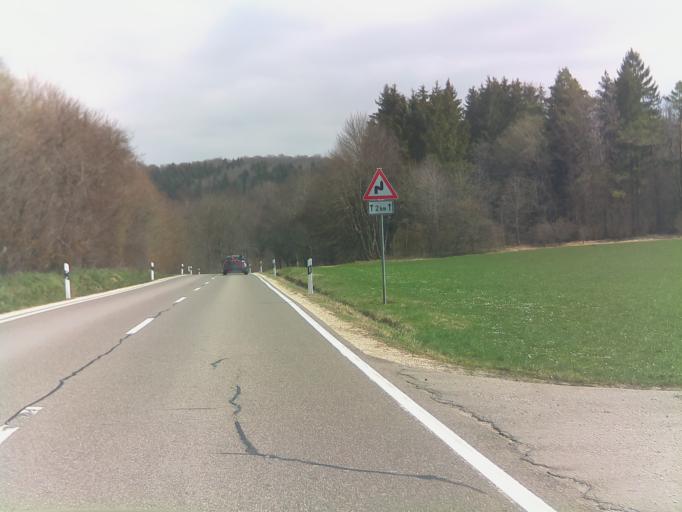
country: DE
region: Baden-Wuerttemberg
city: Altes Lager
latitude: 48.4117
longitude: 9.5643
